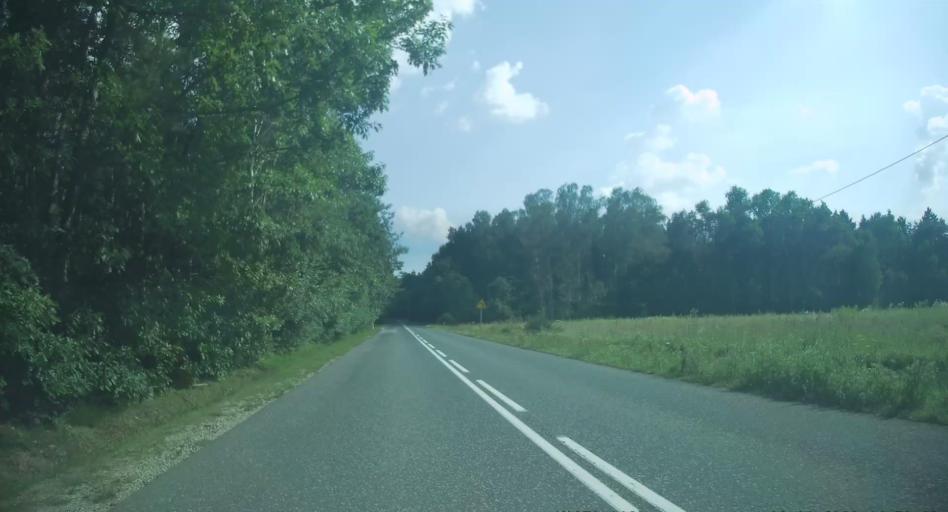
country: PL
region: Swietokrzyskie
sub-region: Powiat kielecki
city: Lopuszno
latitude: 50.8902
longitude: 20.2576
